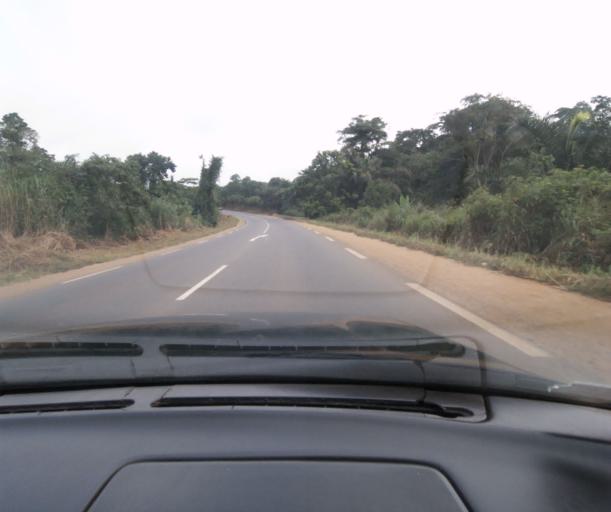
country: CM
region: Centre
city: Obala
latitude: 4.0923
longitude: 11.5426
